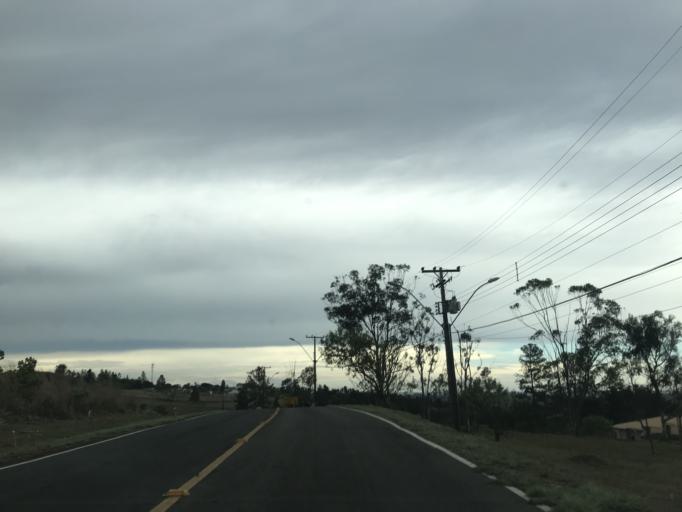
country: BR
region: Federal District
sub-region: Brasilia
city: Brasilia
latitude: -15.9043
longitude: -47.9145
